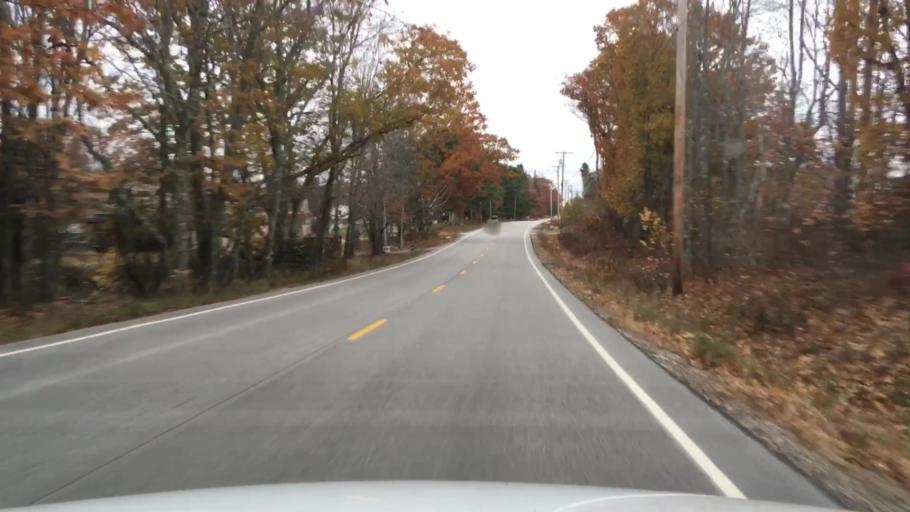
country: US
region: Maine
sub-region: Hancock County
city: Orland
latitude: 44.5410
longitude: -68.6836
